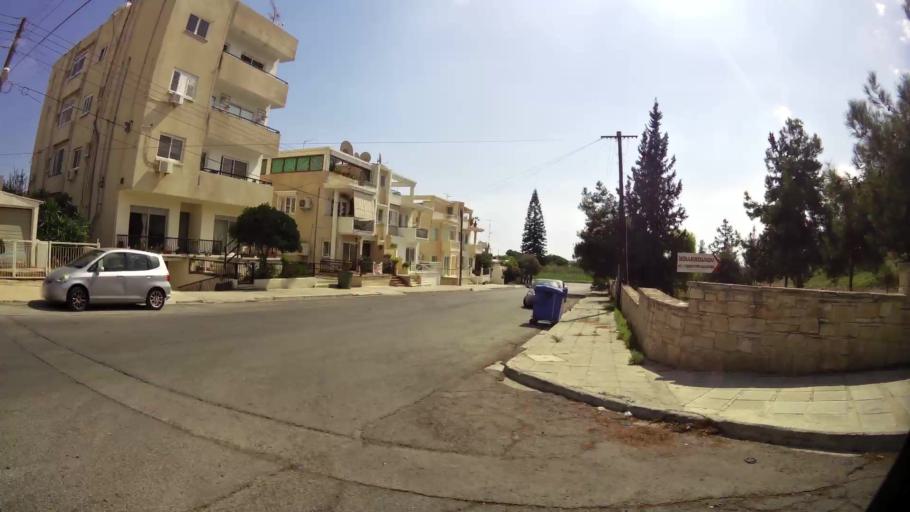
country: CY
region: Larnaka
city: Larnaca
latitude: 34.9129
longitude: 33.6058
